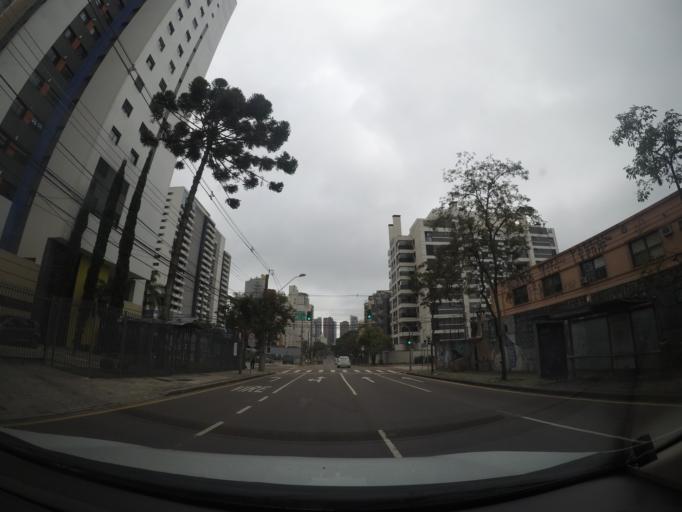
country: BR
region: Parana
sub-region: Curitiba
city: Curitiba
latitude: -25.4175
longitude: -49.2616
